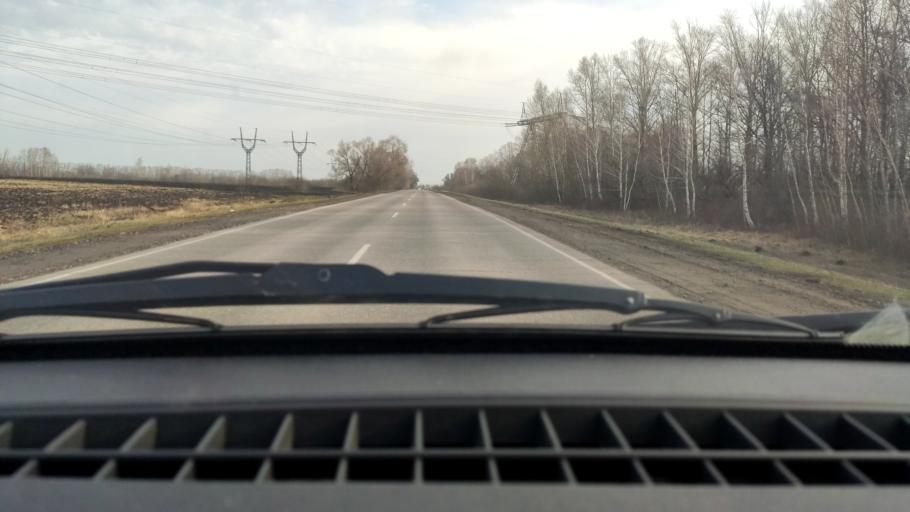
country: RU
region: Bashkortostan
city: Chishmy
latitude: 54.5159
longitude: 55.2950
